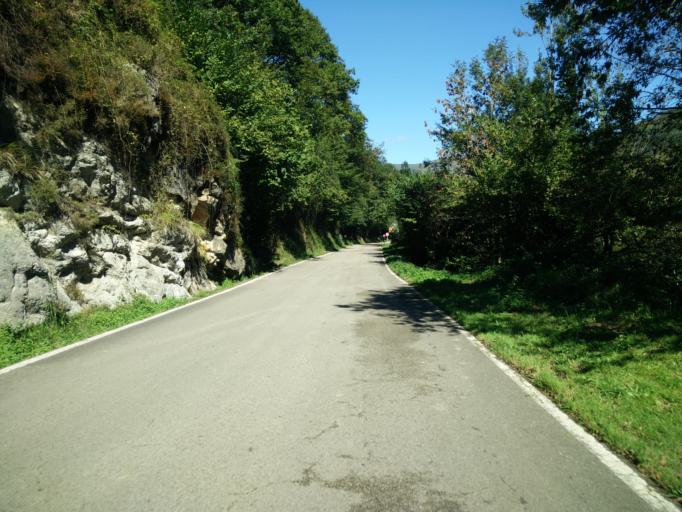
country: ES
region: Cantabria
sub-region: Provincia de Cantabria
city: Ruente
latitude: 43.1401
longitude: -4.2902
